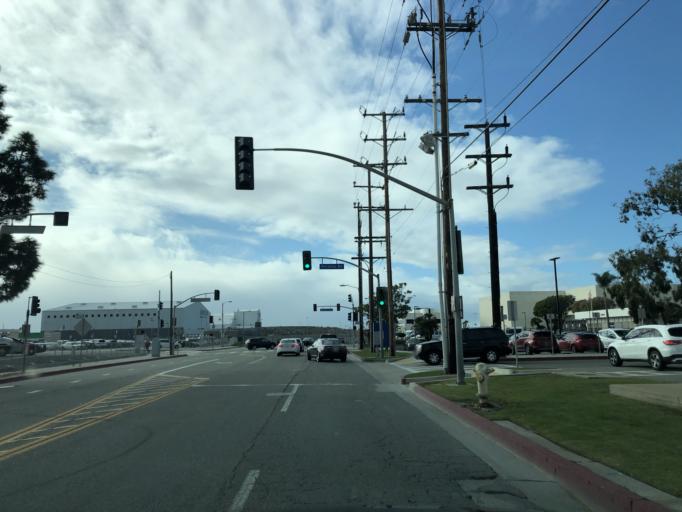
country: US
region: California
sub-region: Los Angeles County
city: El Segundo
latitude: 33.9418
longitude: -118.4238
